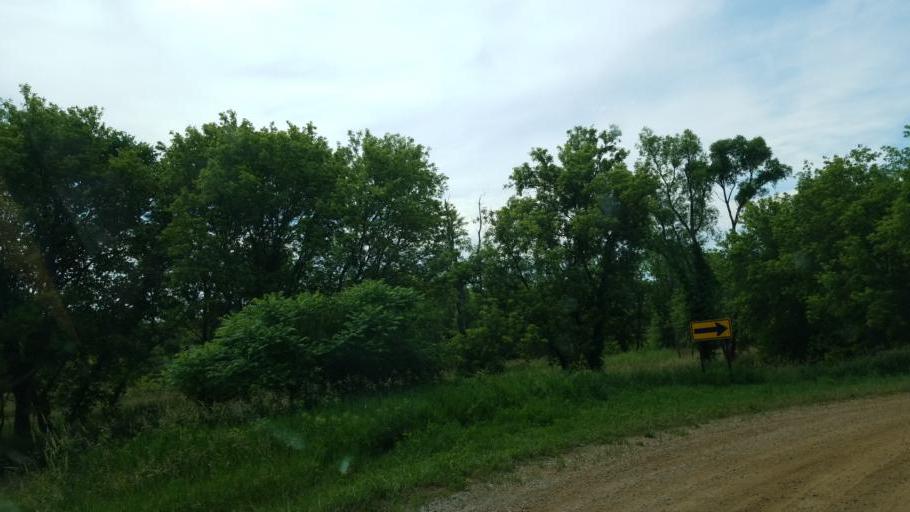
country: US
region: Michigan
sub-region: Eaton County
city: Charlotte
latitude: 42.5897
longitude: -84.8174
